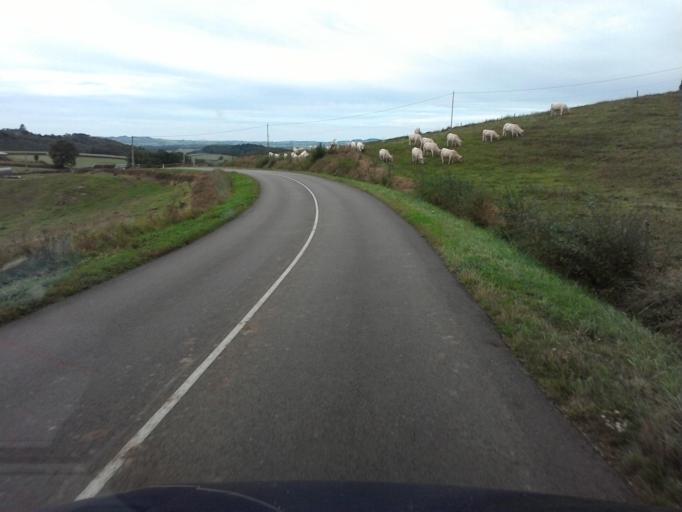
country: FR
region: Bourgogne
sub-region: Departement de Saone-et-Loire
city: Montcenis
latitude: 46.7819
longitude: 4.3858
